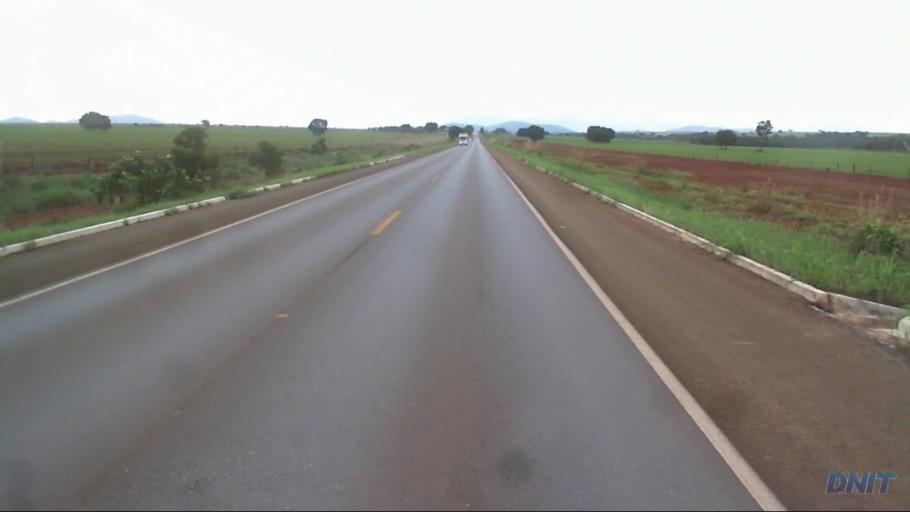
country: BR
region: Goias
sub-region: Barro Alto
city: Barro Alto
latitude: -14.8252
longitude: -49.0373
